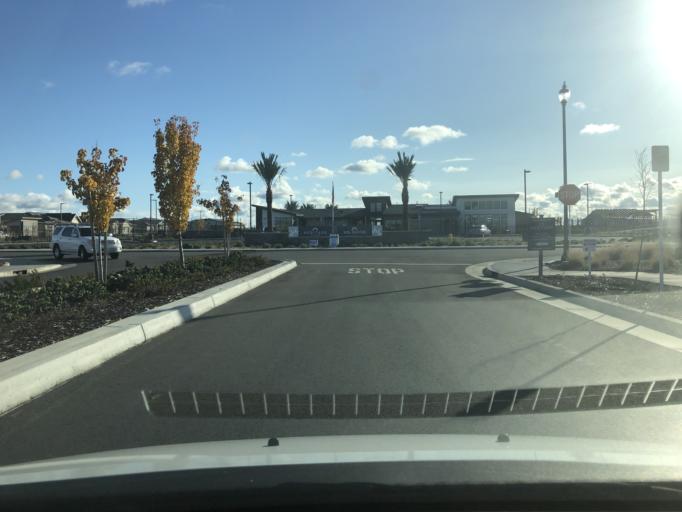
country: US
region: California
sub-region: Sacramento County
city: North Highlands
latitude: 38.7745
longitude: -121.3924
